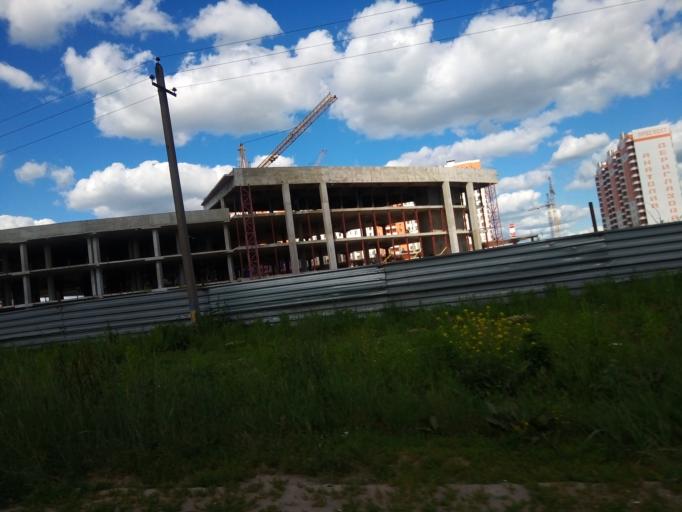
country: RU
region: Kursk
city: Kursk
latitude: 51.8109
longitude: 36.1641
